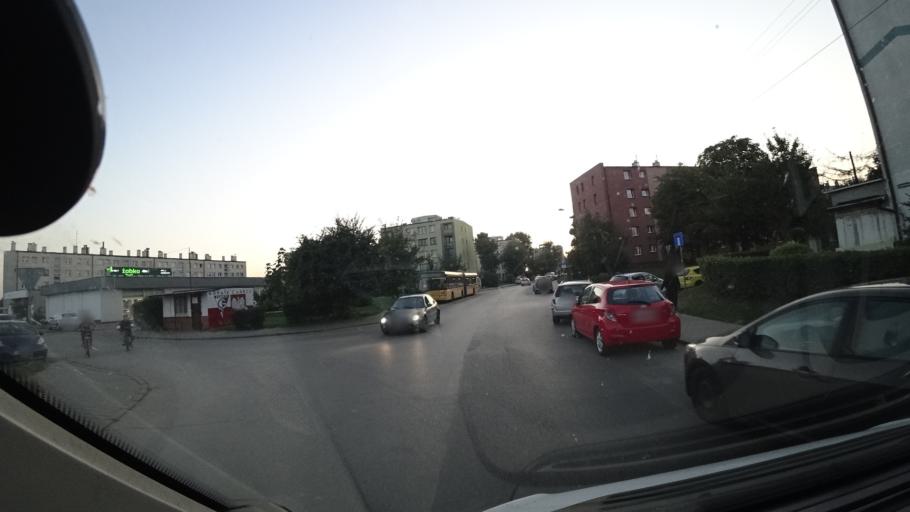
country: PL
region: Silesian Voivodeship
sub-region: Powiat tarnogorski
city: Wieszowa
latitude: 50.3645
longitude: 18.7863
